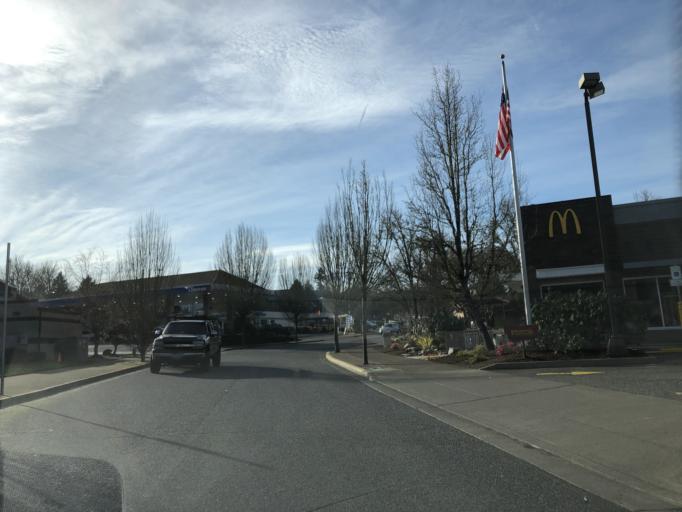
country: US
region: Oregon
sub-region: Clackamas County
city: West Linn
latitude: 45.3463
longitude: -122.6507
